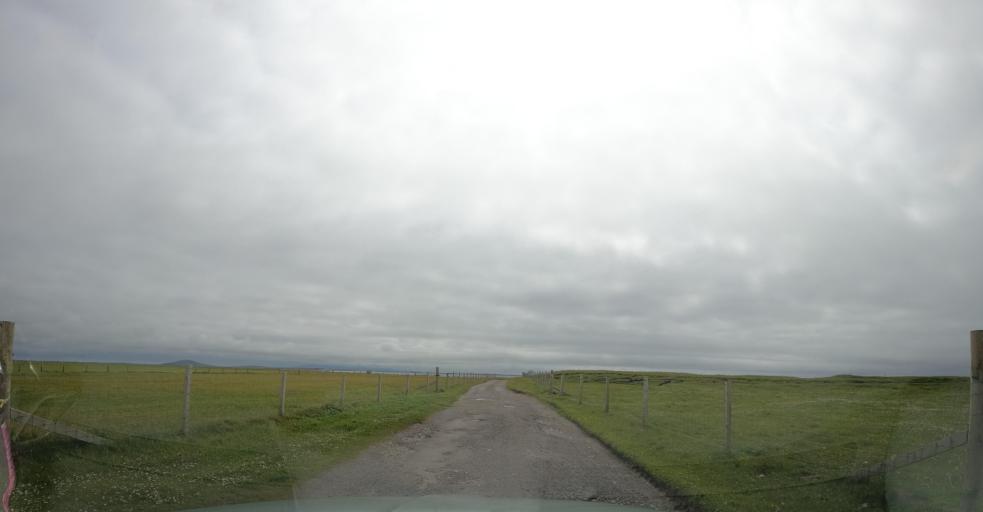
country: GB
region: Scotland
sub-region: Eilean Siar
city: Isle of North Uist
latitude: 57.5289
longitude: -7.3821
